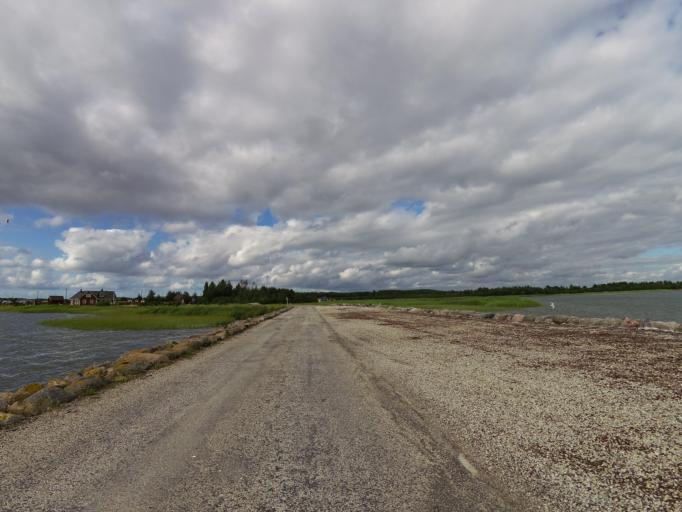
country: EE
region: Laeaene
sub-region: Vormsi vald
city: Hullo
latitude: 58.9716
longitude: 23.3133
